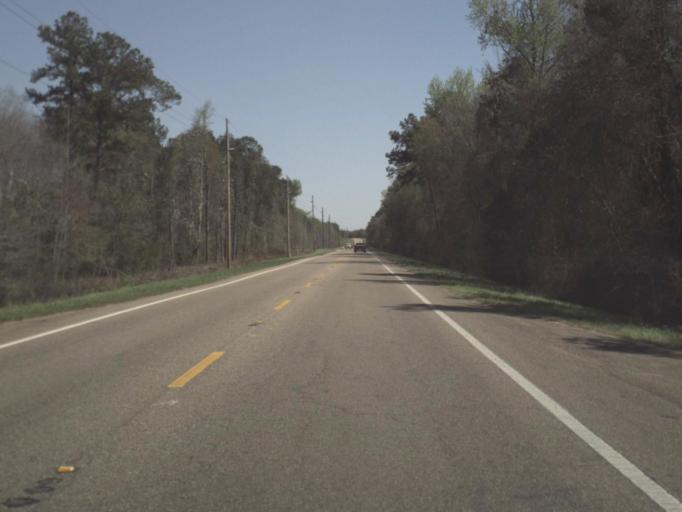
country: US
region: Florida
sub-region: Liberty County
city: Bristol
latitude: 30.4291
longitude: -84.9353
